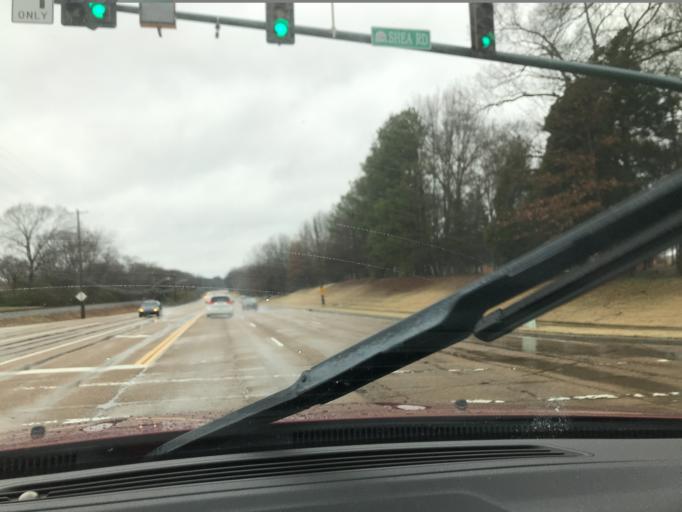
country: US
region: Tennessee
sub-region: Shelby County
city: Collierville
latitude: 35.0472
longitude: -89.7119
